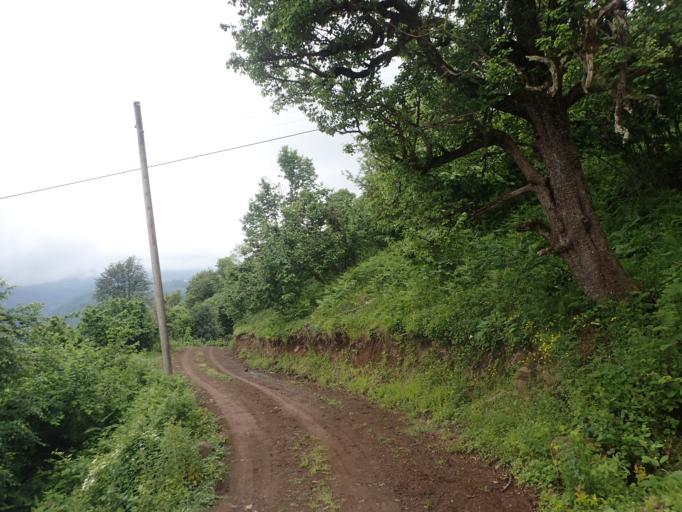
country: TR
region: Samsun
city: Salipazari
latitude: 40.9453
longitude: 36.8941
